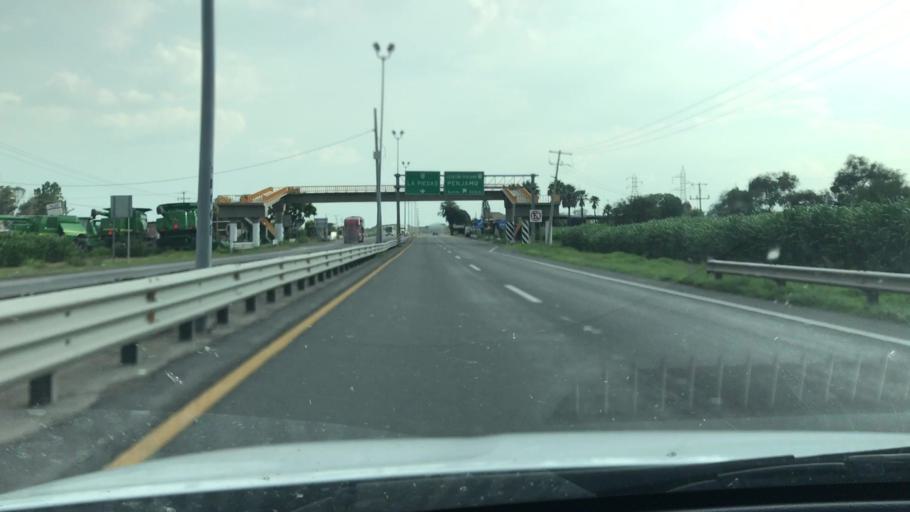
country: MX
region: Guanajuato
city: Penjamo
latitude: 20.4266
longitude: -101.7092
